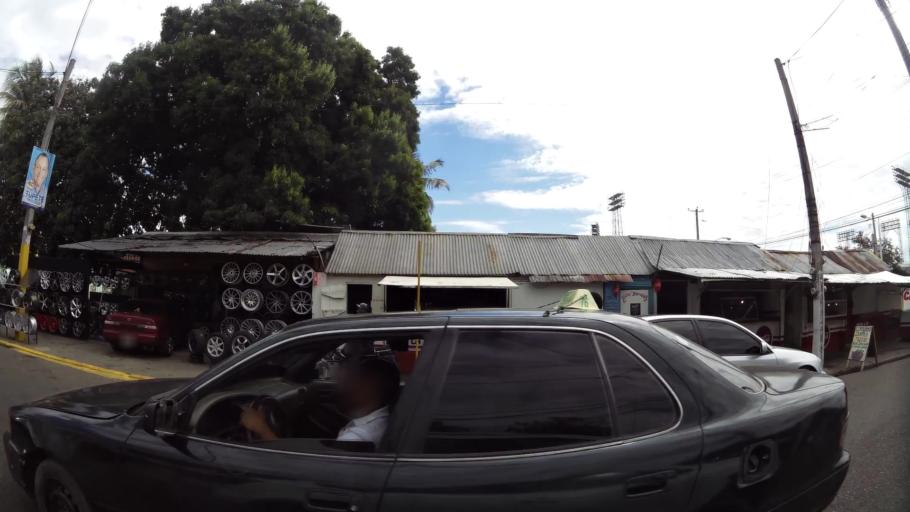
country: DO
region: Santiago
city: Santiago de los Caballeros
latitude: 19.4686
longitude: -70.7101
